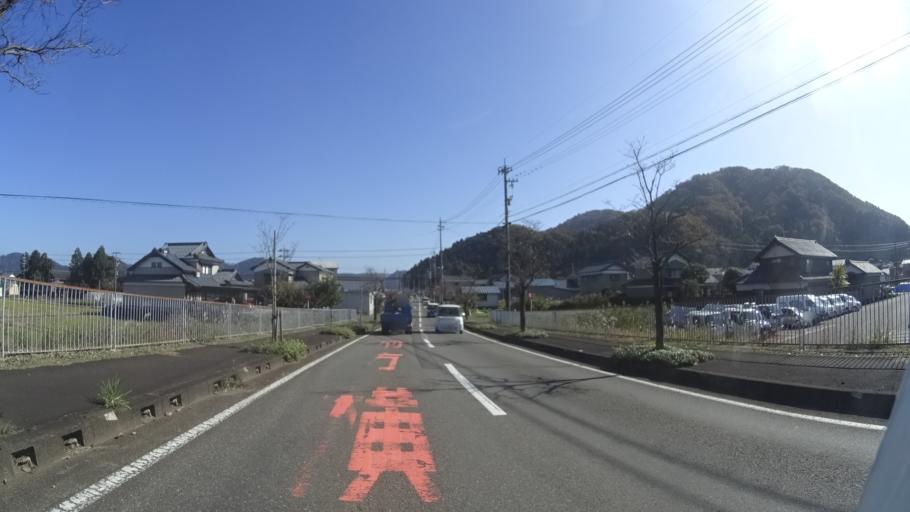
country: JP
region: Fukui
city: Sabae
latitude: 35.9496
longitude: 136.2081
